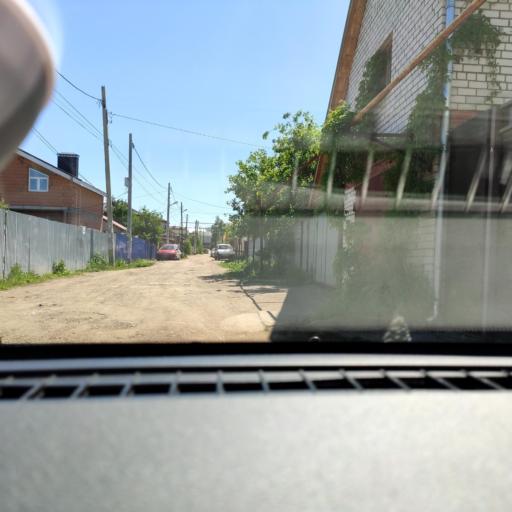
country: RU
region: Samara
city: Samara
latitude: 53.2707
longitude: 50.2027
